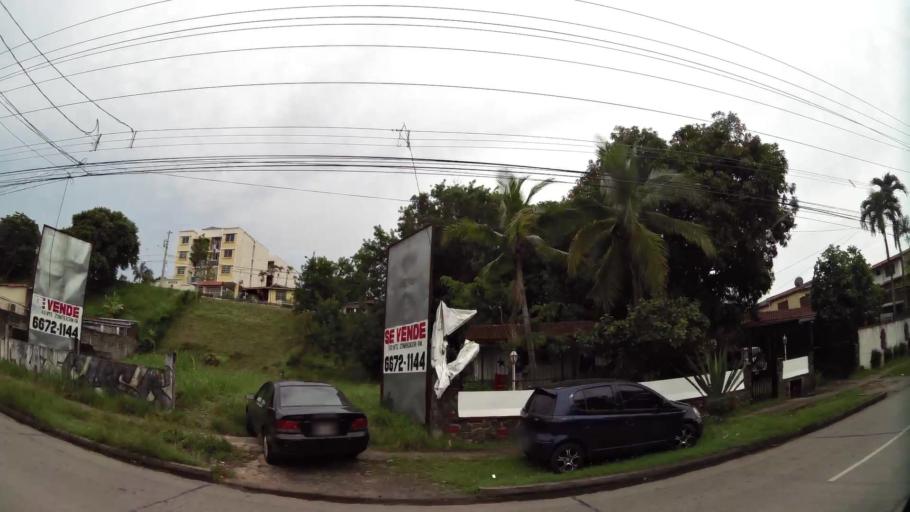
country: PA
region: Panama
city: Panama
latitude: 9.0240
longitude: -79.5187
